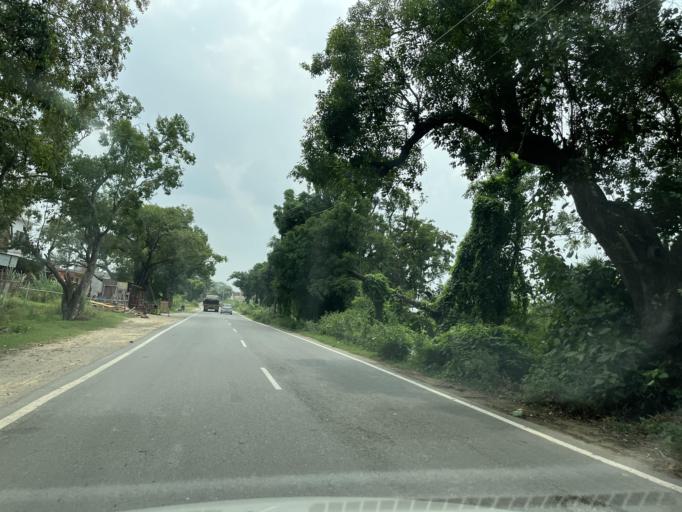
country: IN
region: Uttar Pradesh
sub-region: Bijnor
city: Najibabad
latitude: 29.5857
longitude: 78.3386
